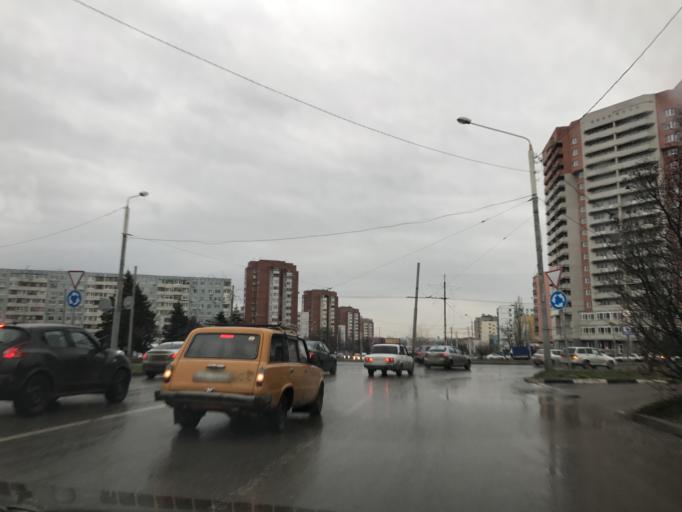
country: RU
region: Rostov
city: Severnyy
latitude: 47.2961
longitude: 39.7130
